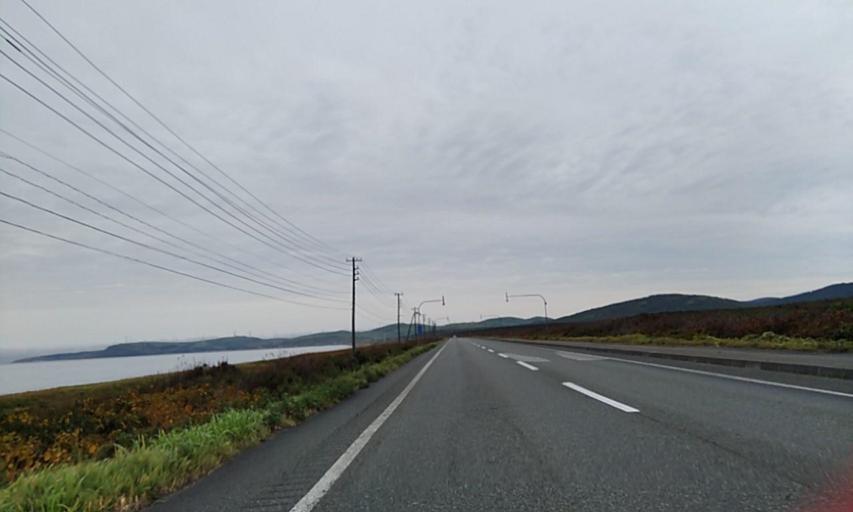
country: JP
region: Hokkaido
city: Makubetsu
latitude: 45.4173
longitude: 141.8290
